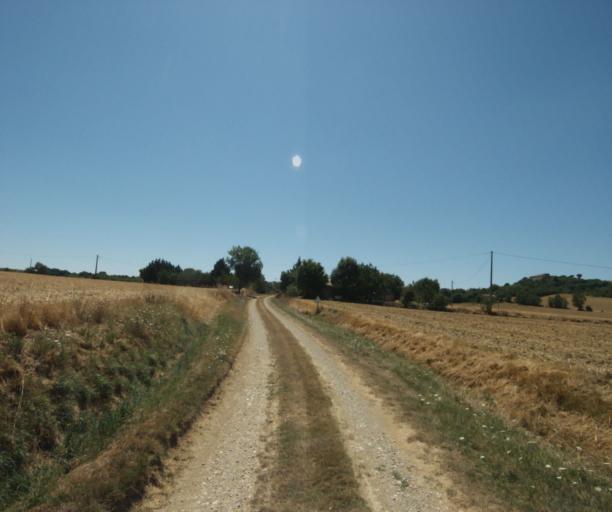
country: FR
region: Midi-Pyrenees
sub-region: Departement de la Haute-Garonne
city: Saint-Felix-Lauragais
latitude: 43.4529
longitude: 1.8992
